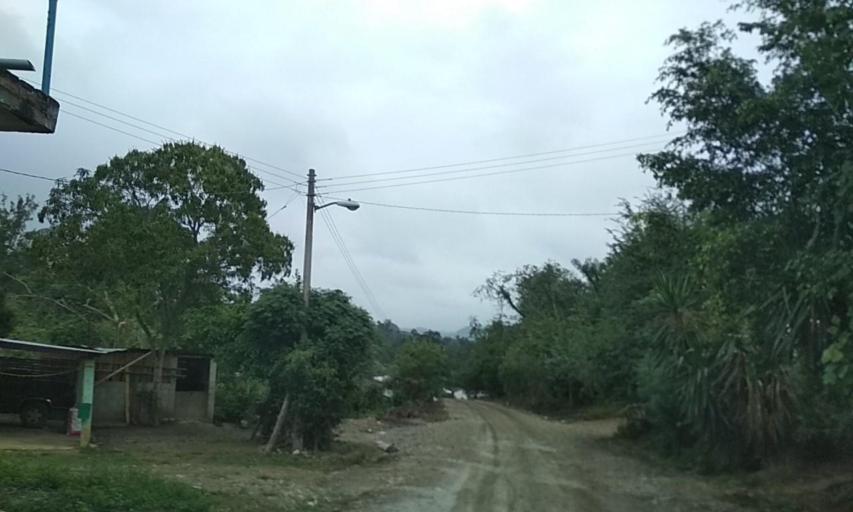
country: MX
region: Veracruz
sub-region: Papantla
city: El Chote
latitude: 20.3810
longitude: -97.3519
